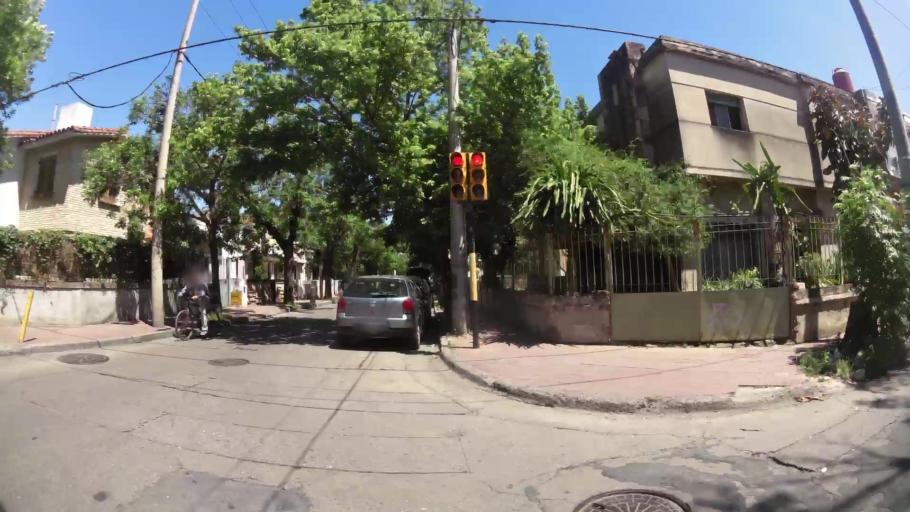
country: AR
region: Cordoba
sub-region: Departamento de Capital
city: Cordoba
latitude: -31.4119
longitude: -64.2021
